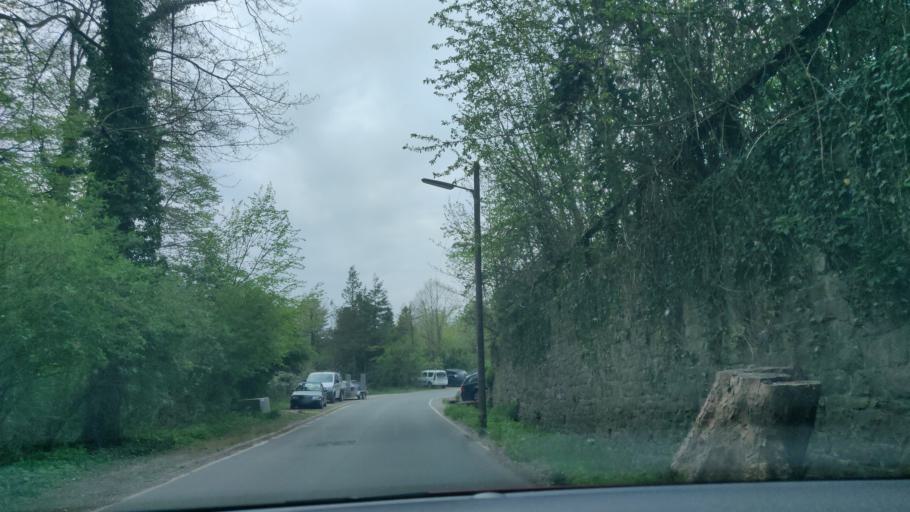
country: DE
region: North Rhine-Westphalia
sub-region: Regierungsbezirk Dusseldorf
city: Velbert
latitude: 51.3940
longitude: 7.0415
